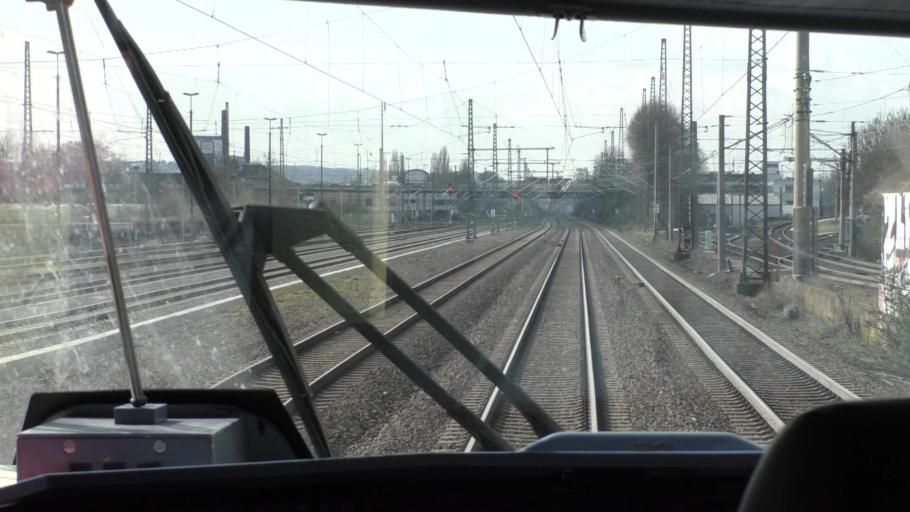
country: DE
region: North Rhine-Westphalia
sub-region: Regierungsbezirk Koln
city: Bonn
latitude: 50.7364
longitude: 7.0822
